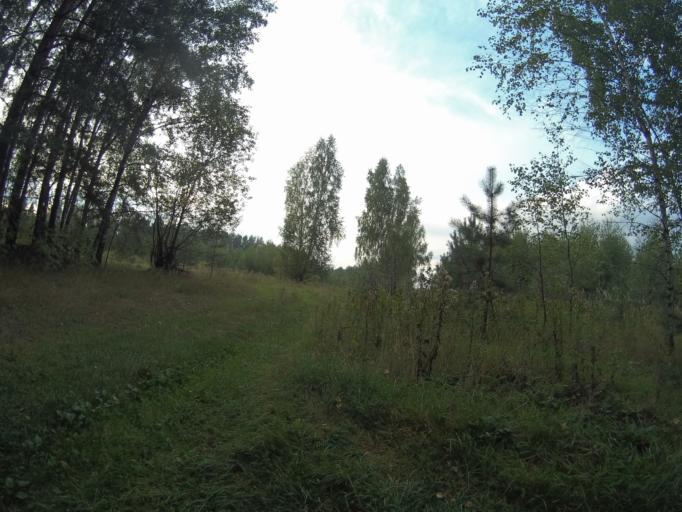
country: RU
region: Vladimir
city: Raduzhnyy
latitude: 55.9910
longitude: 40.2685
